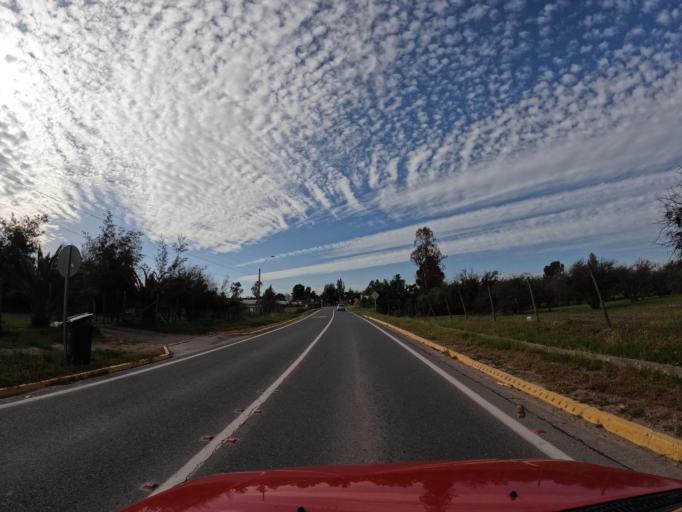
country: CL
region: O'Higgins
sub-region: Provincia de Colchagua
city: Santa Cruz
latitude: -34.2443
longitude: -71.7271
